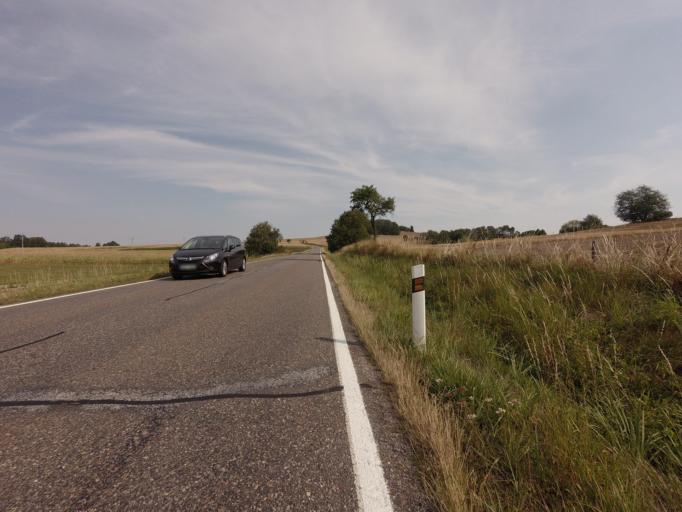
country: CZ
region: Jihocesky
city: Milevsko
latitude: 49.5055
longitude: 14.3637
